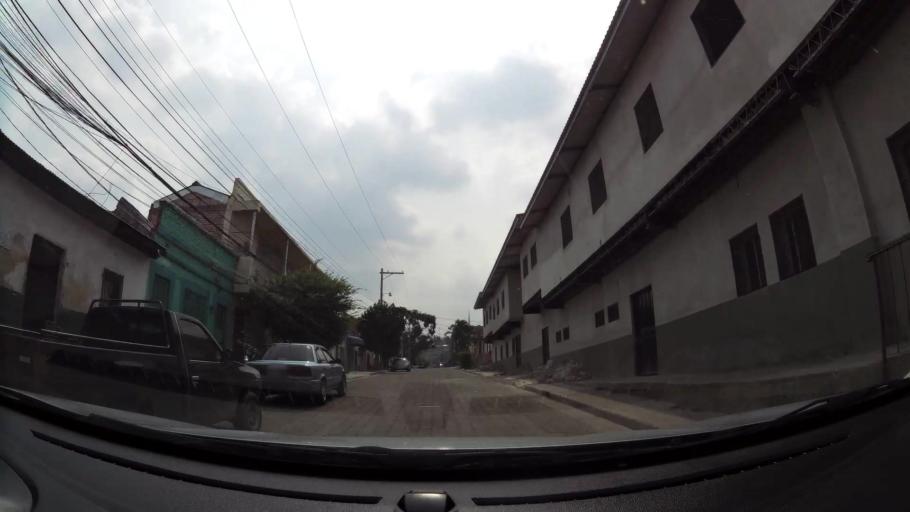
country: HN
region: Francisco Morazan
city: Tegucigalpa
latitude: 14.0904
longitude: -87.2115
